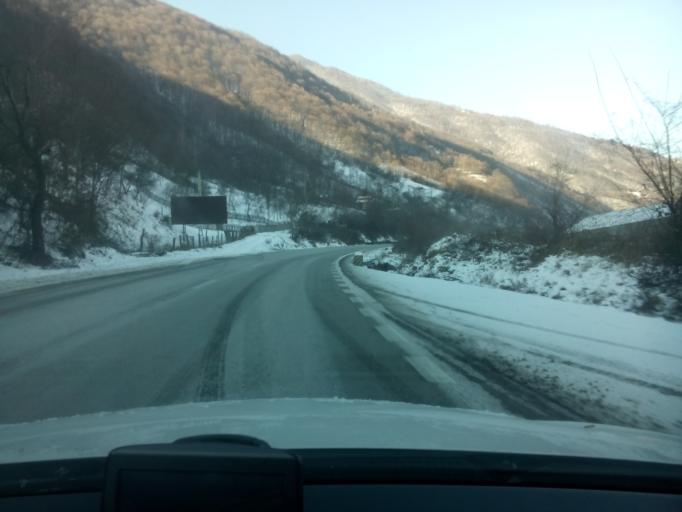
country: RO
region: Valcea
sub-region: Comuna Caineni
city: Greblesti
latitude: 45.4554
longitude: 24.2901
